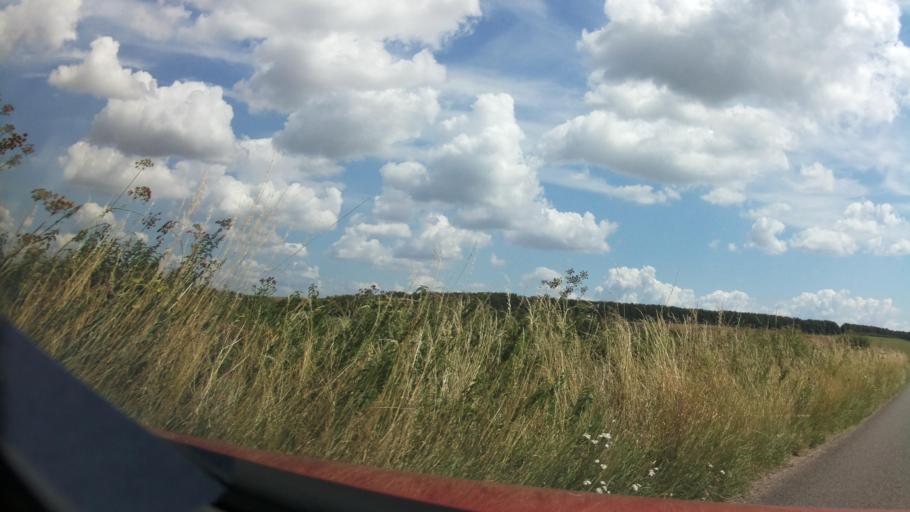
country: GB
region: England
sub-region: Borough of Swindon
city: Bishopstone
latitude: 51.5535
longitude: -1.6030
